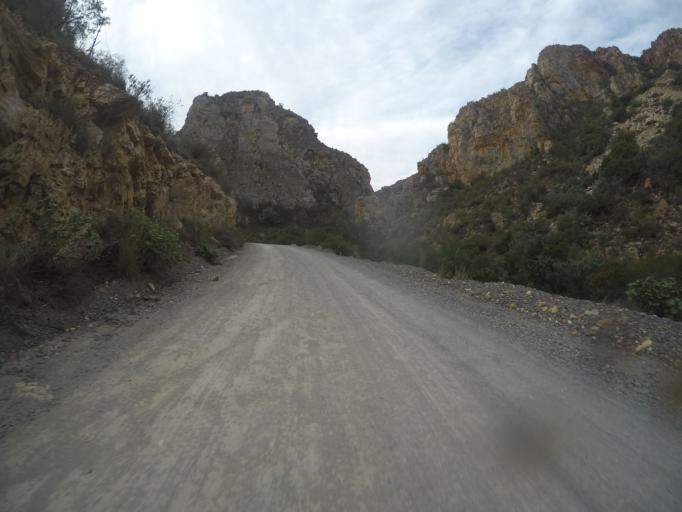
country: ZA
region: Eastern Cape
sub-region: Cacadu District Municipality
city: Willowmore
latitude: -33.5109
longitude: 23.6401
